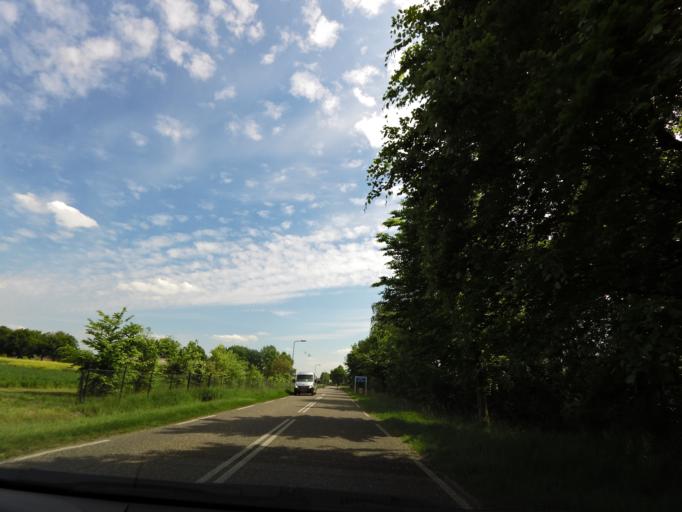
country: NL
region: Limburg
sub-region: Gemeente Leudal
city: Haelen
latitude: 51.2700
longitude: 5.9820
